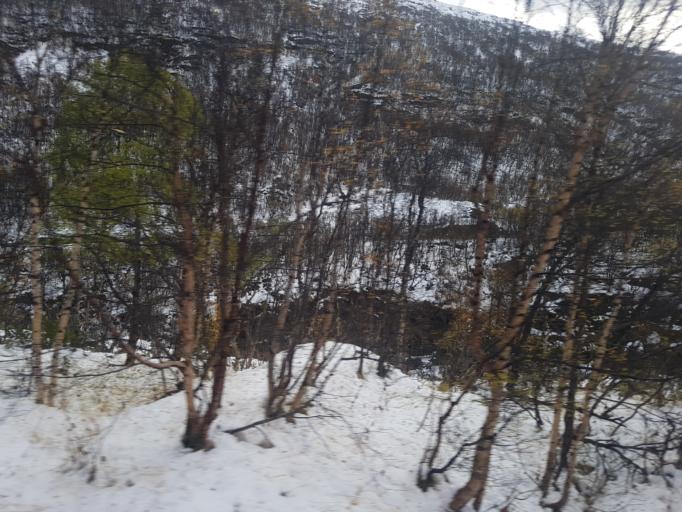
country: NO
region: Sor-Trondelag
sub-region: Oppdal
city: Oppdal
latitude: 62.3394
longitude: 9.6232
